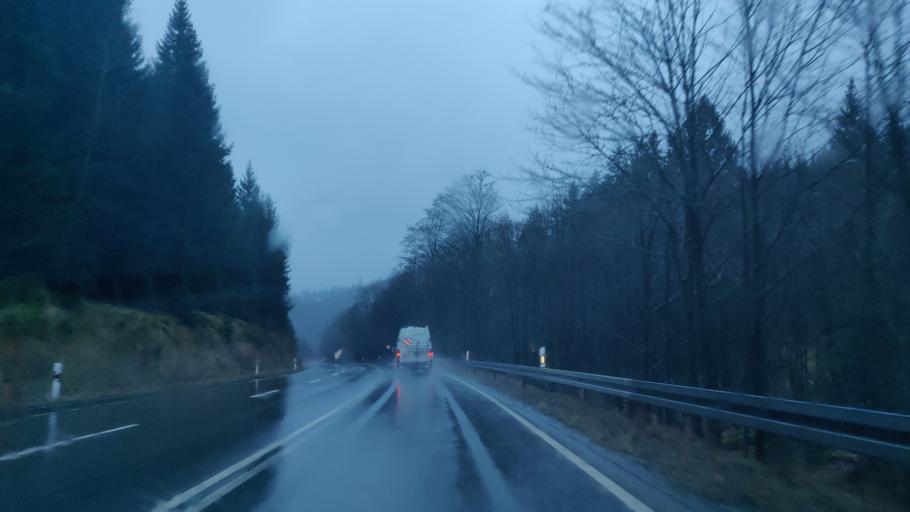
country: DE
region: Lower Saxony
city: Braunlage
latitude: 51.7032
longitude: 10.5832
